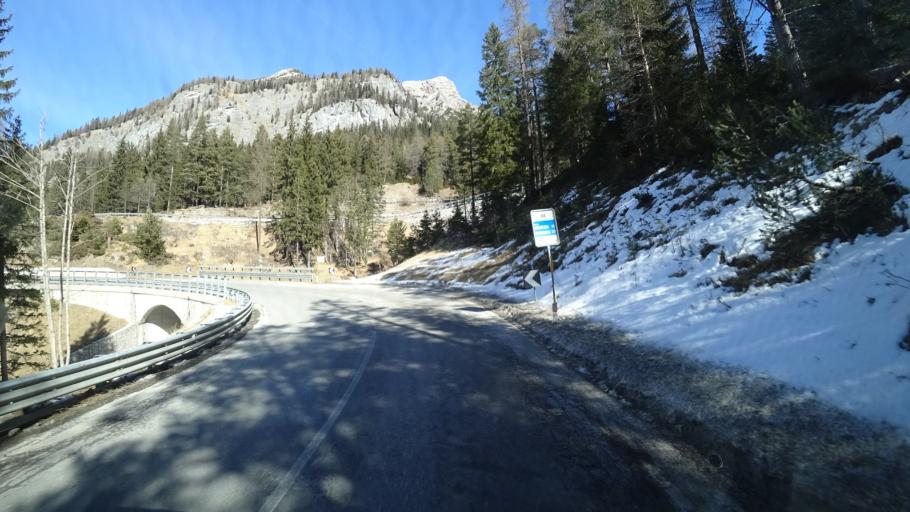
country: IT
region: Veneto
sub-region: Provincia di Belluno
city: Cortina d'Ampezzo
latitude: 46.6021
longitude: 12.1109
